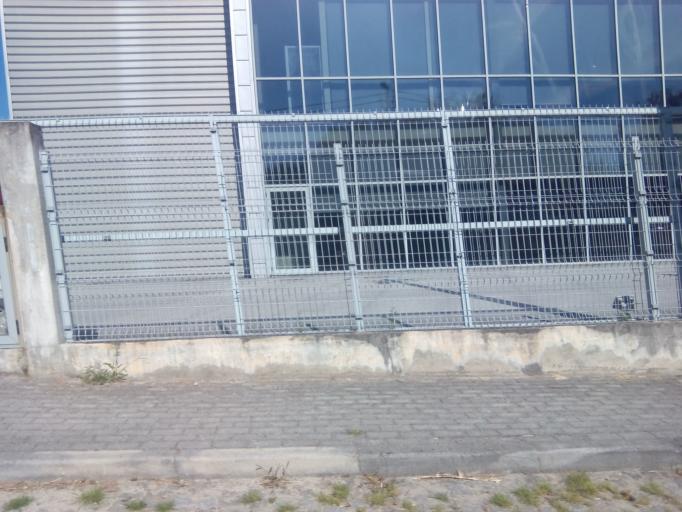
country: PT
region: Porto
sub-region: Paredes
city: Casteloes de Cepeda
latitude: 41.1934
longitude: -8.3424
